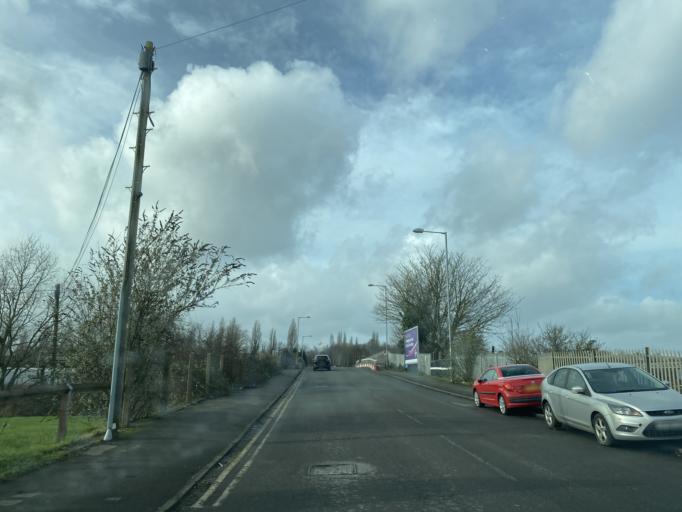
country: GB
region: England
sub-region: Walsall
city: Walsall
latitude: 52.5788
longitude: -1.9902
